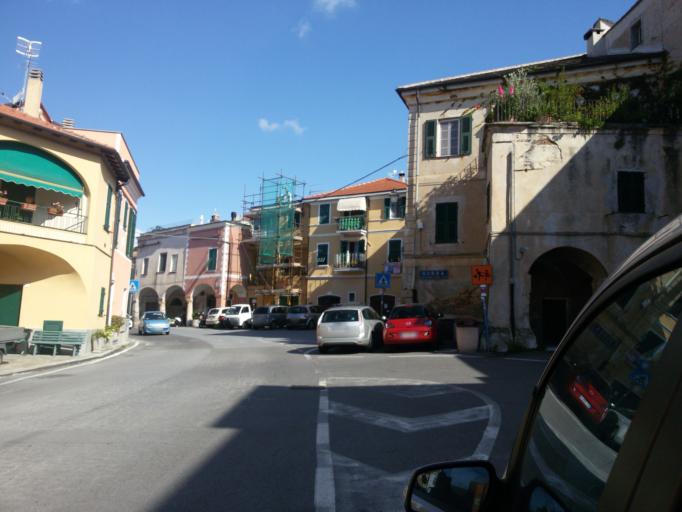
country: IT
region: Liguria
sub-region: Provincia di Savona
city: Calice Ligure
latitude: 44.1827
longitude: 8.2980
